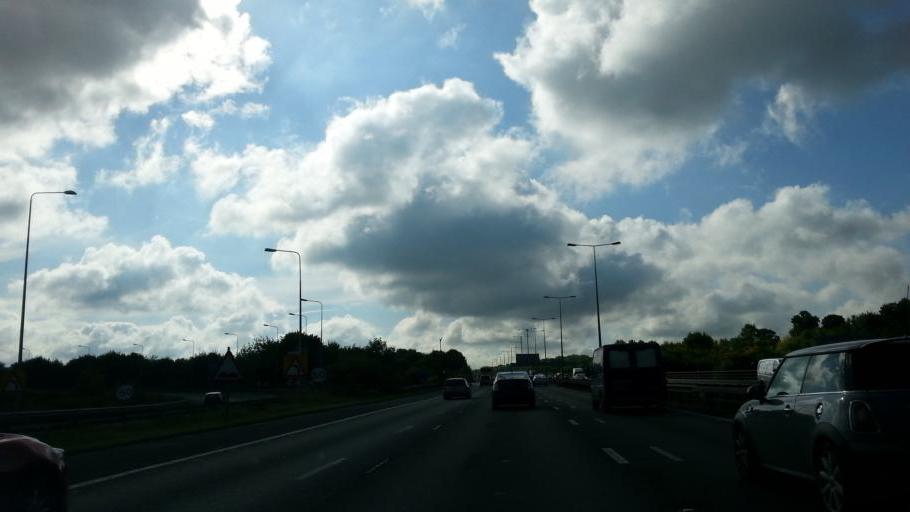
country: GB
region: England
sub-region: Buckinghamshire
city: Denham
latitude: 51.5589
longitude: -0.5302
